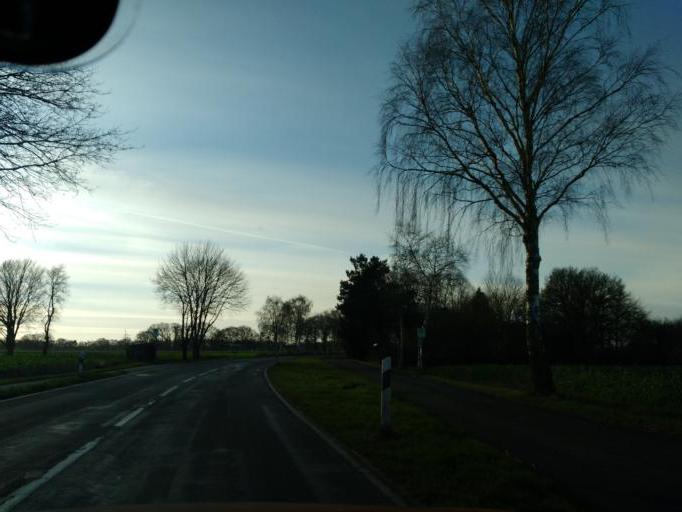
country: DE
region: Lower Saxony
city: Hatten
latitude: 53.0889
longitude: 8.4050
